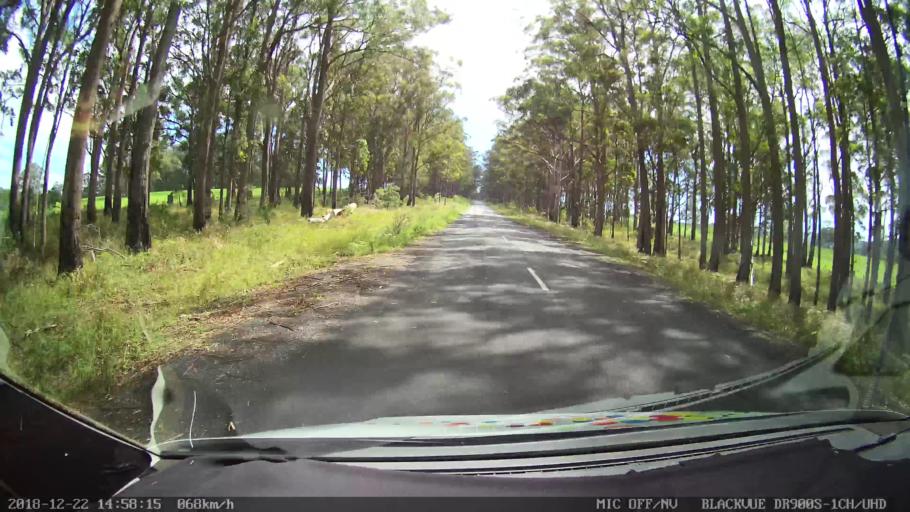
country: AU
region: New South Wales
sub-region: Bellingen
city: Dorrigo
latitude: -30.2390
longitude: 152.4930
